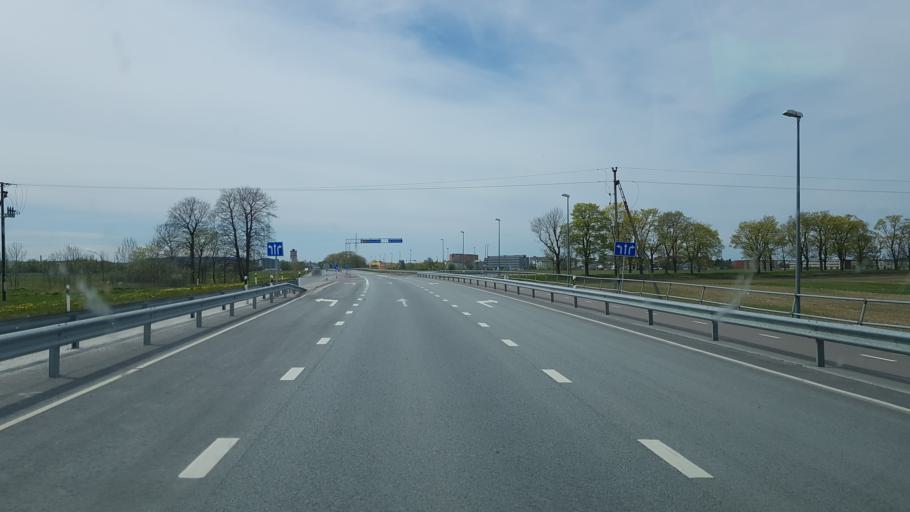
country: EE
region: Ida-Virumaa
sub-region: Kohtla-Jaerve linn
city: Kohtla-Jarve
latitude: 59.4036
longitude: 27.3141
